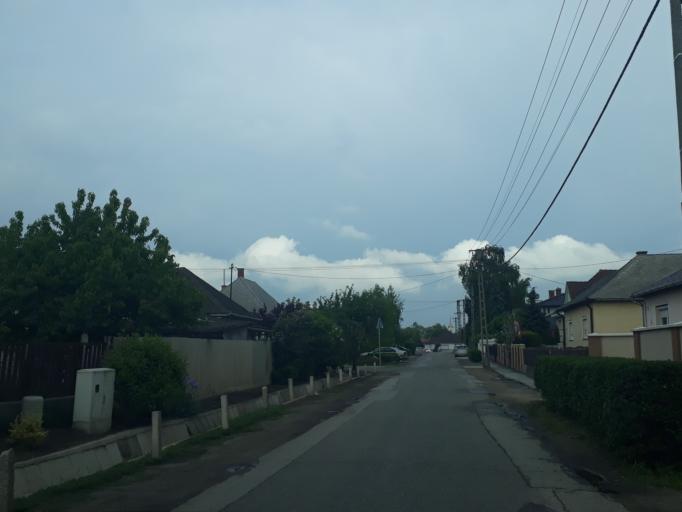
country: HU
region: Szabolcs-Szatmar-Bereg
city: Kisvarda
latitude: 48.2187
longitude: 22.0717
